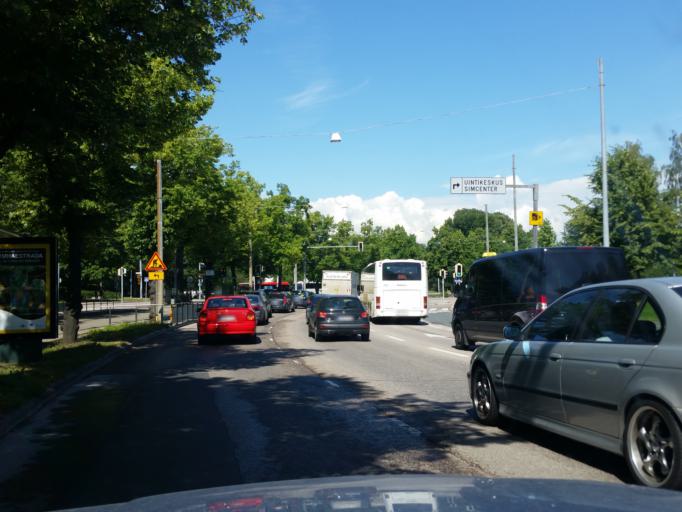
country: FI
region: Uusimaa
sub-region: Helsinki
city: Helsinki
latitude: 60.1998
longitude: 24.9457
